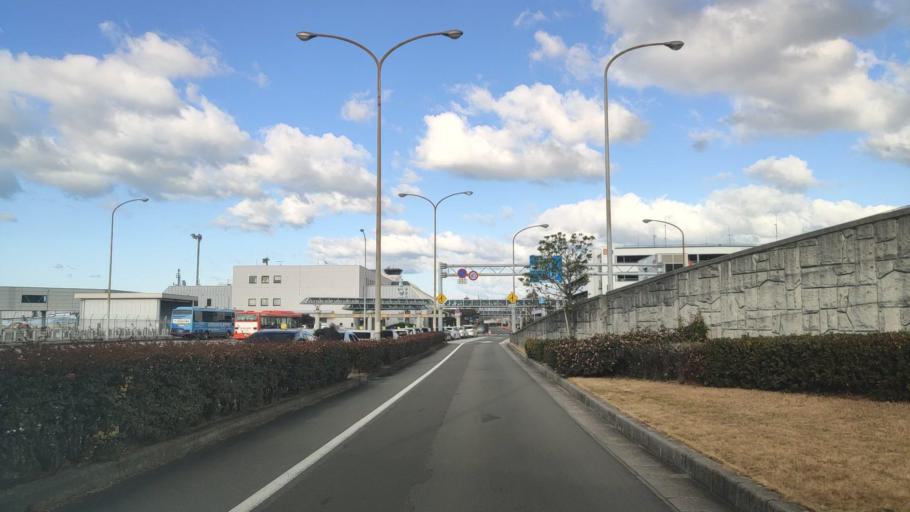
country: JP
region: Ehime
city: Masaki-cho
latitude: 33.8280
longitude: 132.7063
